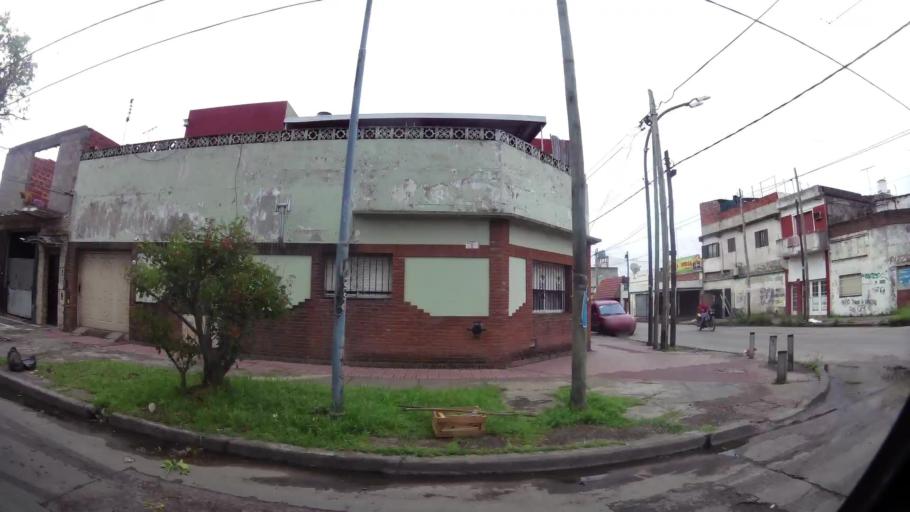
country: AR
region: Buenos Aires
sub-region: Partido de Lanus
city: Lanus
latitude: -34.7202
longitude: -58.3732
